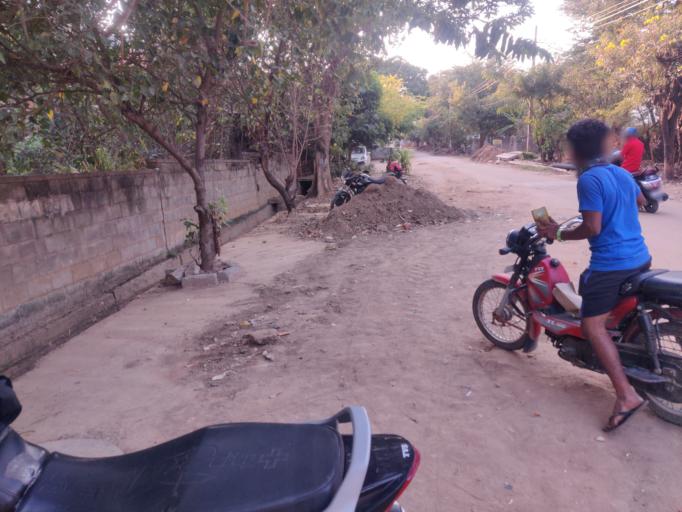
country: IN
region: Karnataka
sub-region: Bangalore Urban
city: Bangalore
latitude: 12.9141
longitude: 77.6709
